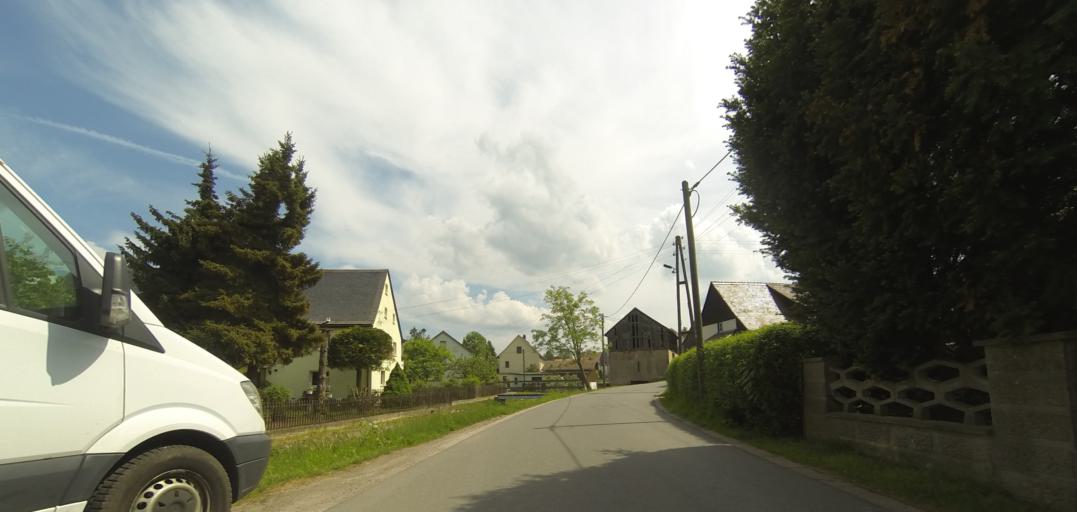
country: DE
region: Saxony
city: Grossrohrsdorf
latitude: 51.1016
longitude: 14.0340
